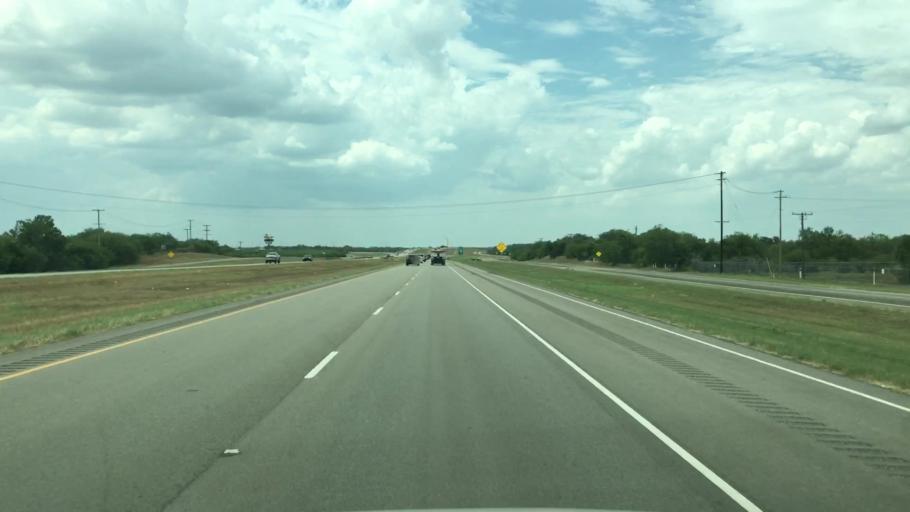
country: US
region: Texas
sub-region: Live Oak County
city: Three Rivers
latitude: 28.5158
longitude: -98.1748
